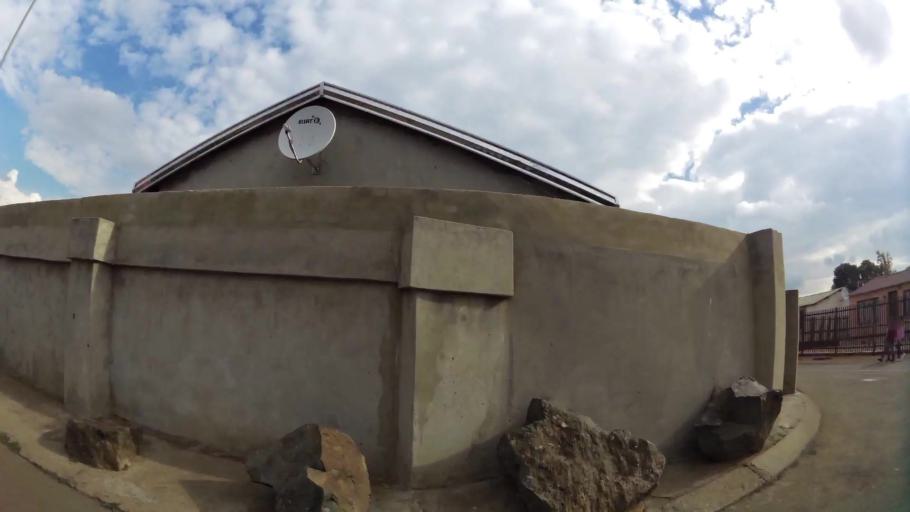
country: ZA
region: Gauteng
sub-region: City of Johannesburg Metropolitan Municipality
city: Soweto
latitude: -26.2370
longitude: 27.8658
